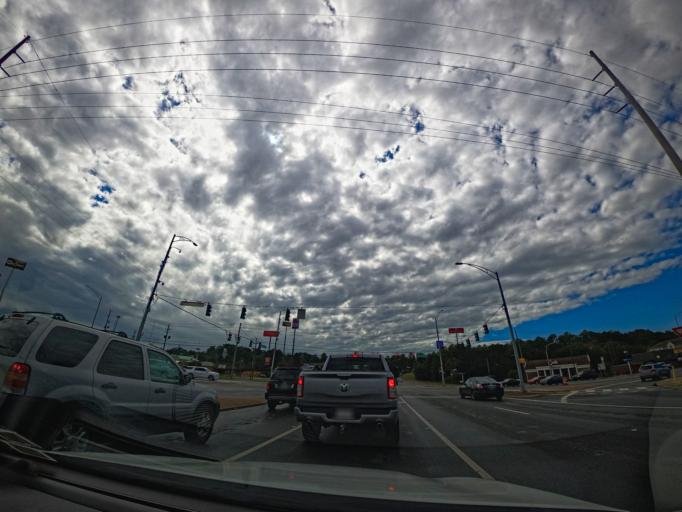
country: US
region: Alabama
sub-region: Tuscaloosa County
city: Tuscaloosa
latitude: 33.1686
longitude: -87.5255
